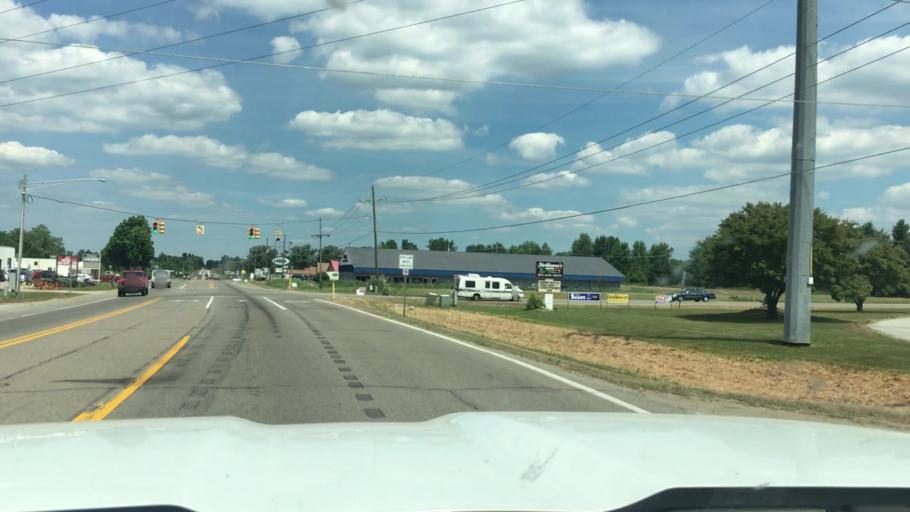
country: US
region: Michigan
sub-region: Lapeer County
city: Lapeer
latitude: 43.0867
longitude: -83.3074
